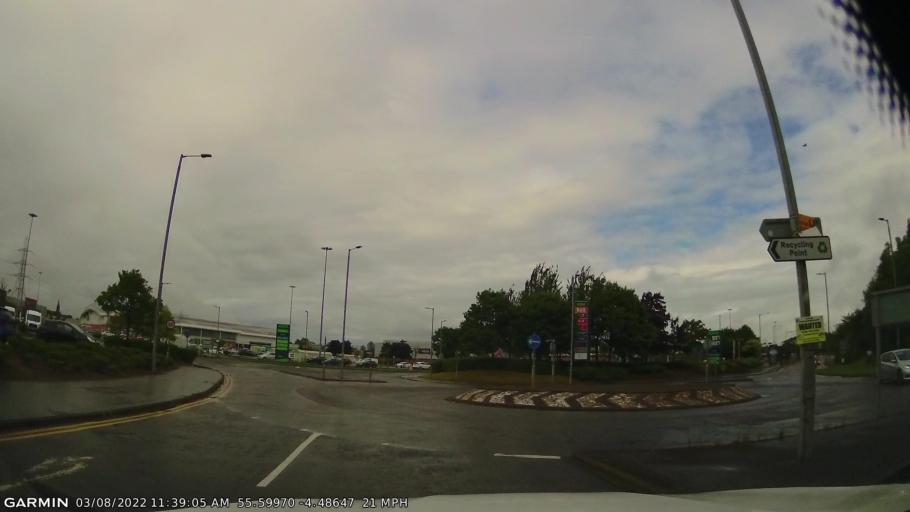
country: GB
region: Scotland
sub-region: East Ayrshire
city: Kilmarnock
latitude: 55.5995
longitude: -4.4861
